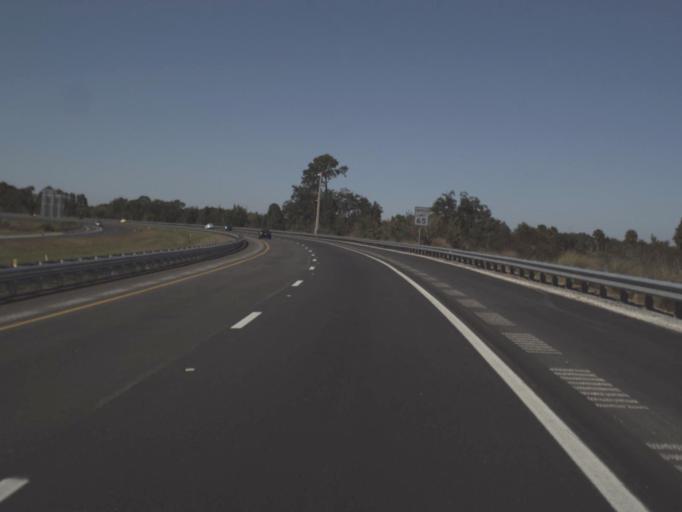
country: US
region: Florida
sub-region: Seminole County
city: Sanford
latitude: 28.7968
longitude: -81.3037
